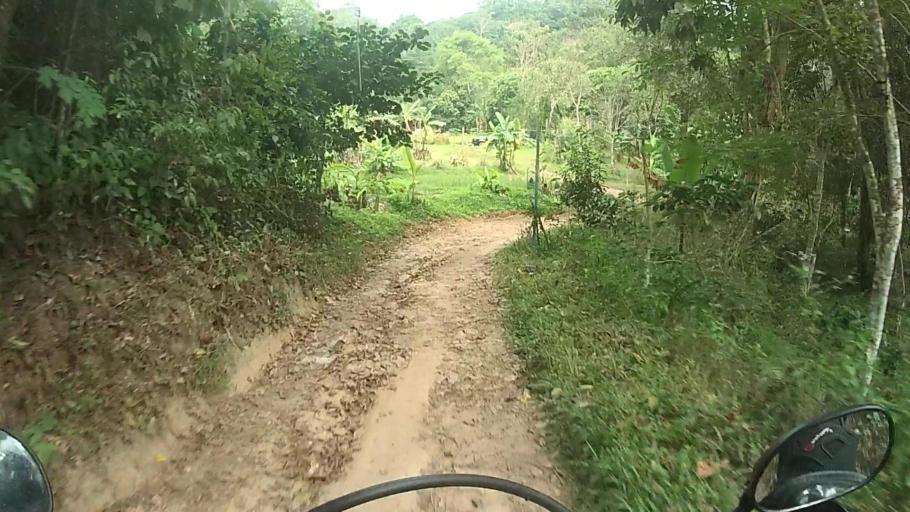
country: TH
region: Lampang
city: Mueang Pan
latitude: 18.8213
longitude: 99.3794
